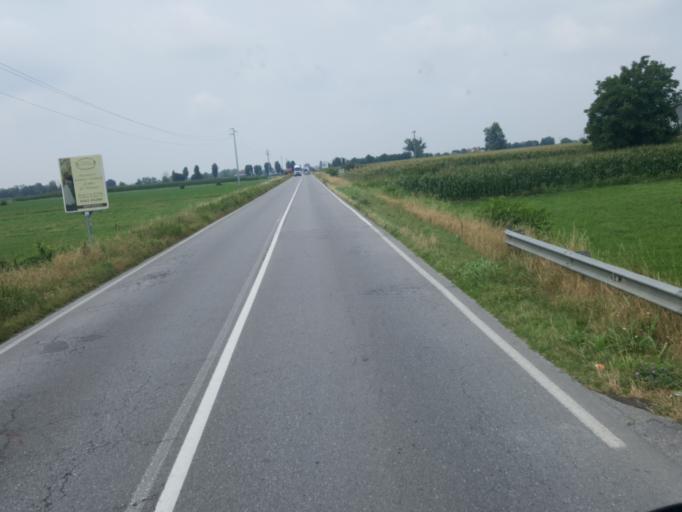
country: IT
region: Lombardy
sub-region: Provincia di Bergamo
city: Arzago d'Adda
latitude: 45.4772
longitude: 9.5853
